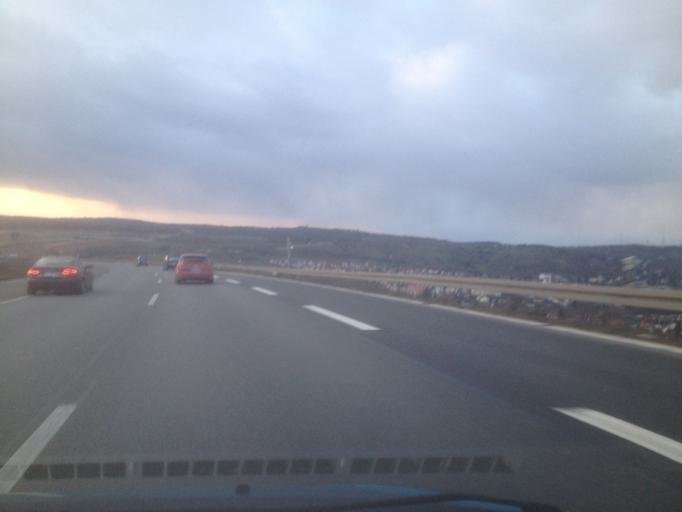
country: DE
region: Bavaria
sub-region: Regierungsbezirk Unterfranken
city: Randersacker
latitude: 49.7556
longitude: 9.9557
